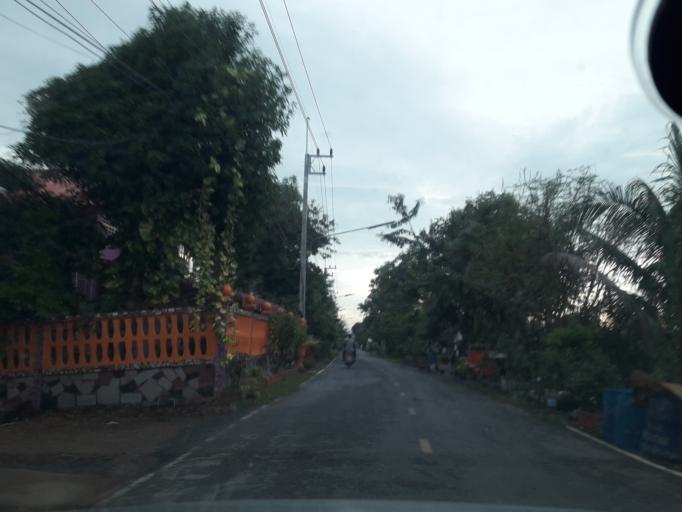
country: TH
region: Phra Nakhon Si Ayutthaya
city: Wang Noi
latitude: 14.2632
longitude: 100.7964
